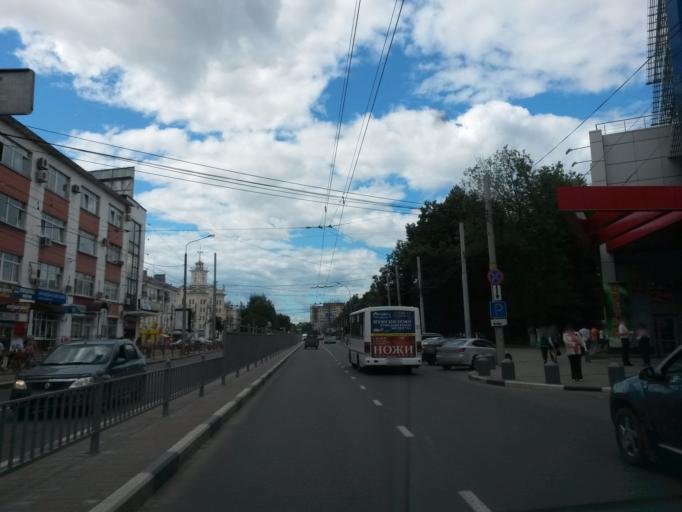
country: RU
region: Jaroslavl
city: Yaroslavl
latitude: 57.6356
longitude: 39.8681
